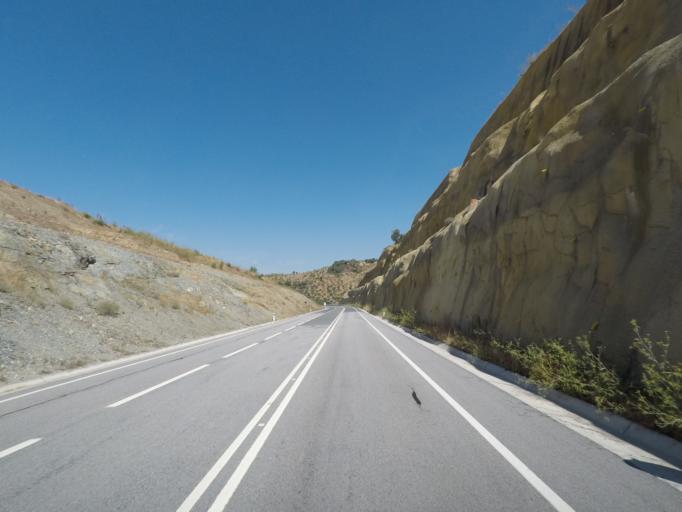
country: PT
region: Braganca
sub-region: Alfandega da Fe
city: Alfandega da Fe
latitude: 41.2920
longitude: -6.8958
